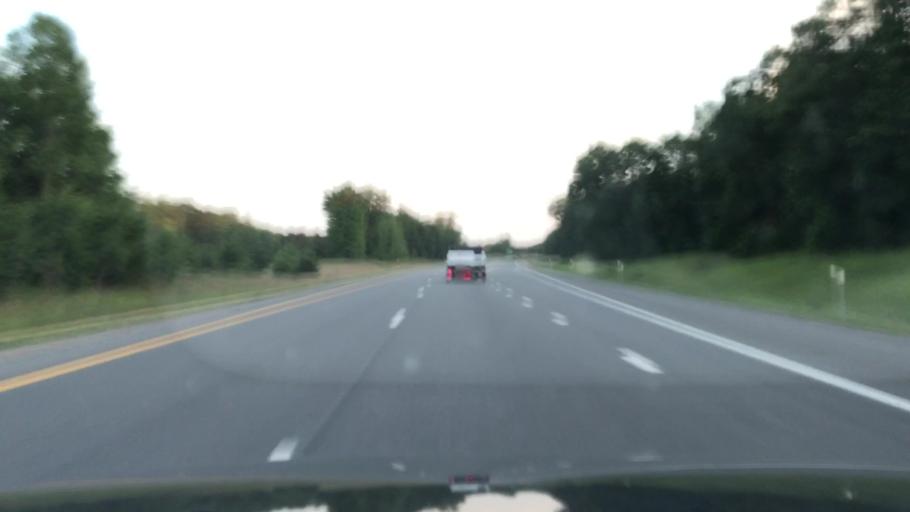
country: US
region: Michigan
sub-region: Montcalm County
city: Howard City
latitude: 43.4323
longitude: -85.4942
